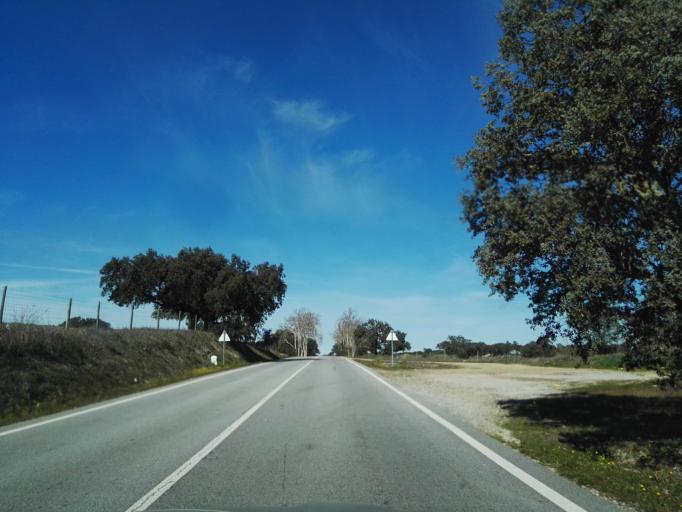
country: PT
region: Portalegre
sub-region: Arronches
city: Arronches
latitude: 39.0602
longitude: -7.2730
